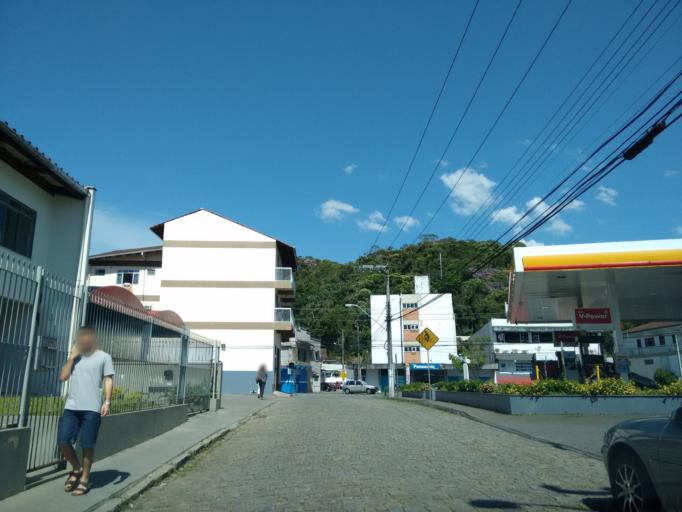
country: BR
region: Santa Catarina
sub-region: Blumenau
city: Blumenau
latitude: -26.9307
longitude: -49.0600
